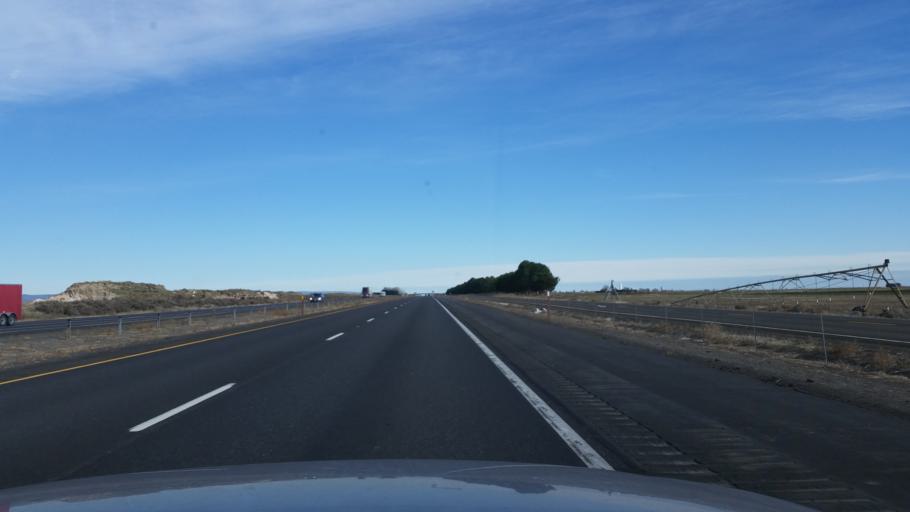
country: US
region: Washington
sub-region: Grant County
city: Quincy
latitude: 47.0572
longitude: -119.8967
